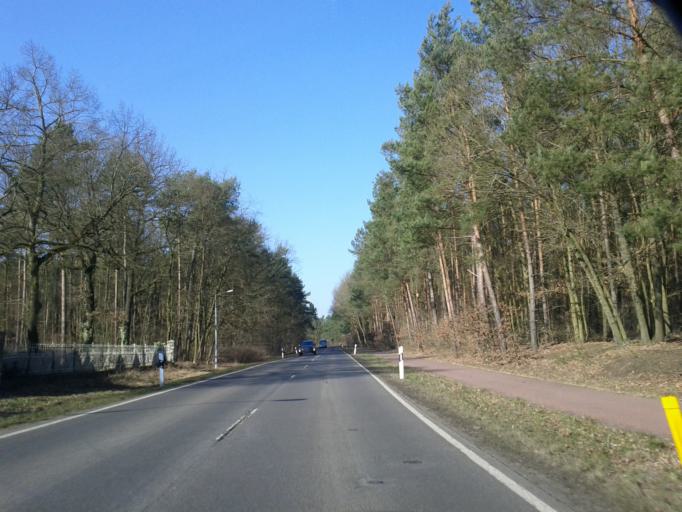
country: DE
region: Brandenburg
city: Grunheide
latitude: 52.4215
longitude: 13.7930
